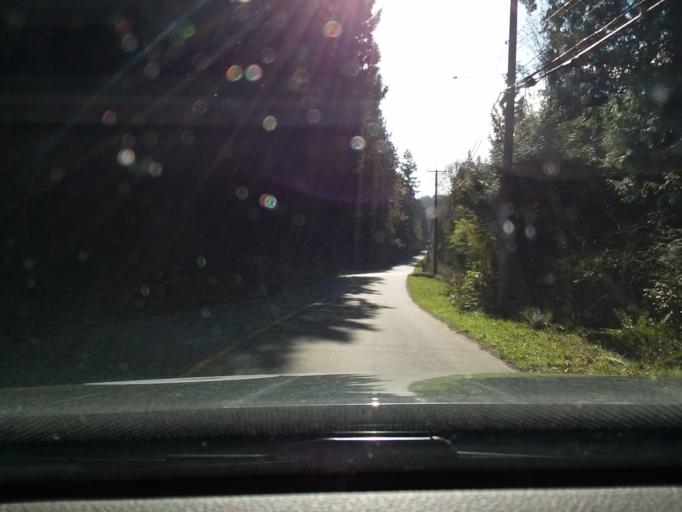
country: CA
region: British Columbia
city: North Cowichan
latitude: 48.9456
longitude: -123.5079
